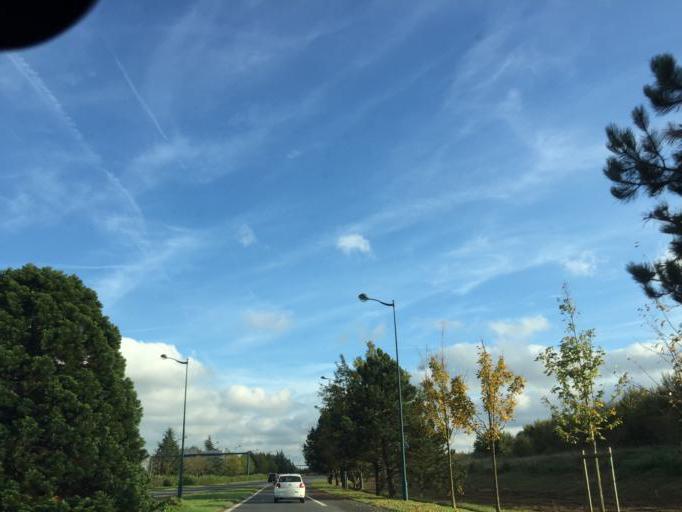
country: FR
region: Ile-de-France
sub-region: Departement de Seine-et-Marne
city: Serris
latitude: 48.8583
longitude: 2.7948
